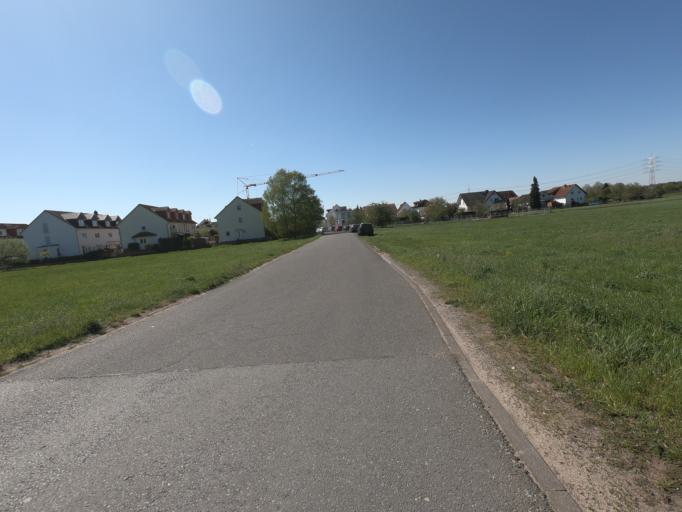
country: DE
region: Hesse
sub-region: Regierungsbezirk Darmstadt
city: Erzhausen
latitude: 49.9553
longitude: 8.6262
